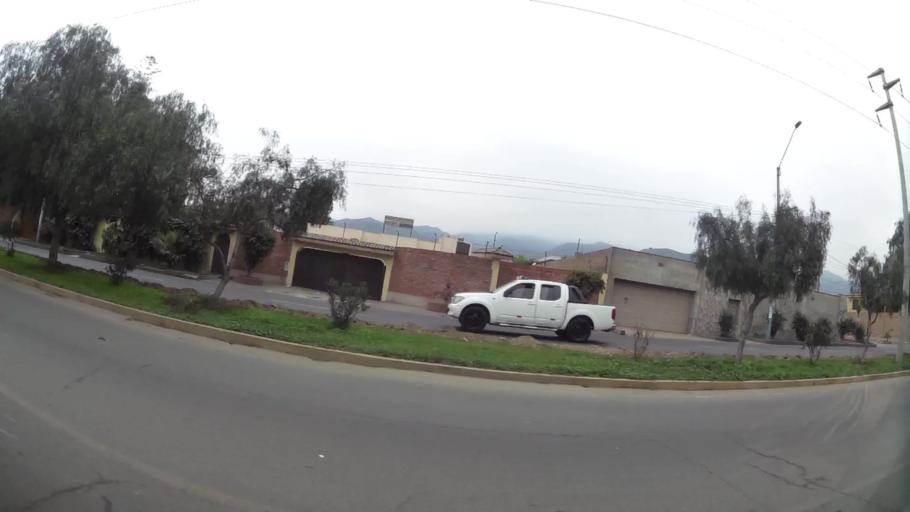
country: PE
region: Lima
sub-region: Lima
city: La Molina
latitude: -12.0861
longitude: -76.8954
